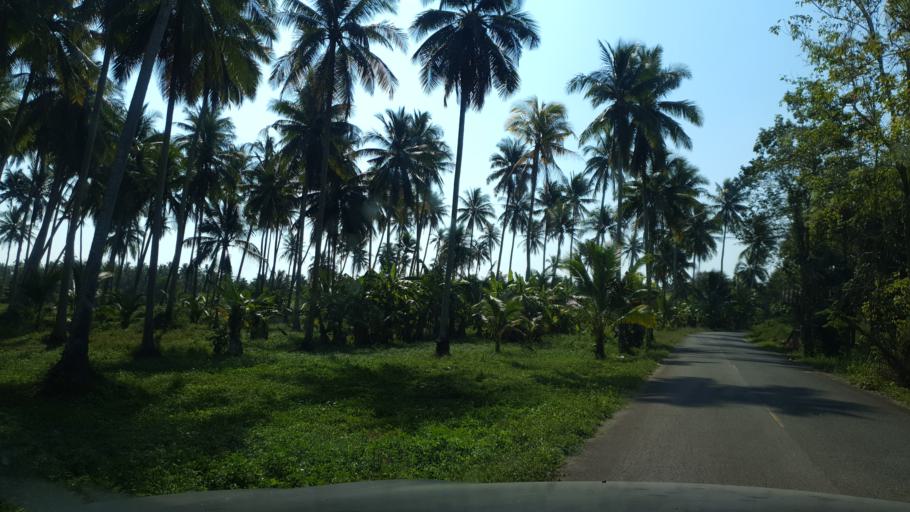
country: TH
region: Prachuap Khiri Khan
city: Thap Sakae
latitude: 11.3629
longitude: 99.5528
